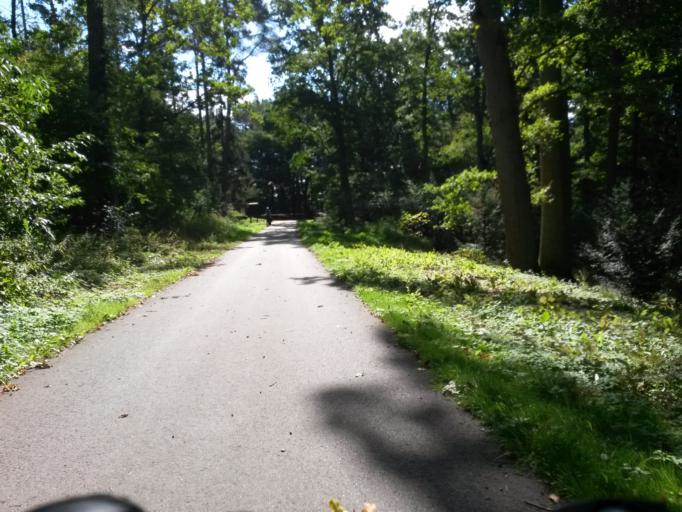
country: DE
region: Brandenburg
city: Lychen
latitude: 53.1634
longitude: 13.4008
